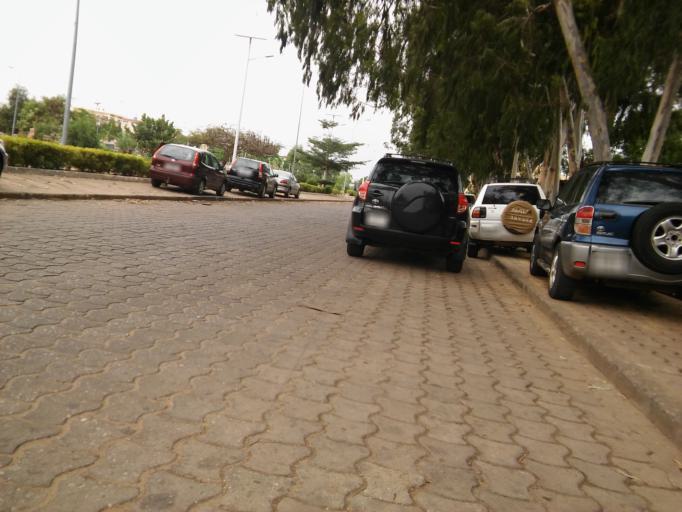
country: BJ
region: Littoral
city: Cotonou
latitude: 6.3541
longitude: 2.4079
